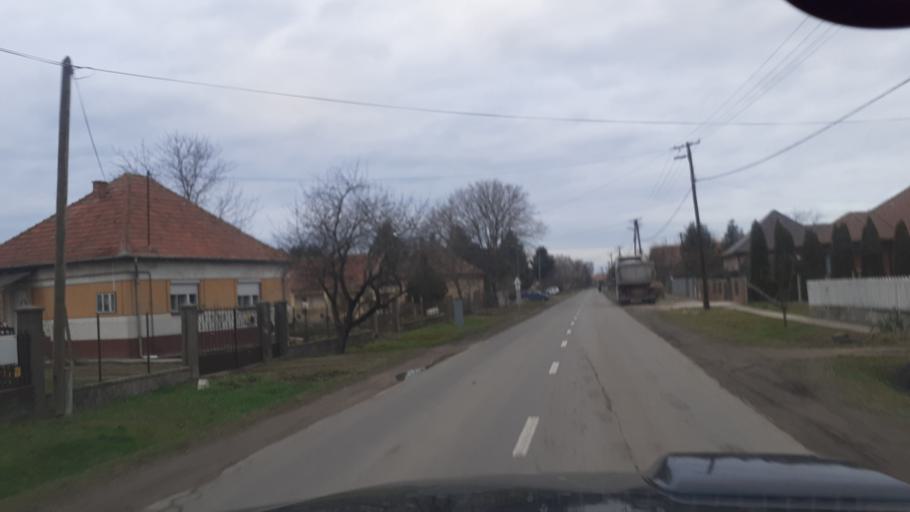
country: HU
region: Bacs-Kiskun
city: Szalkszentmarton
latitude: 46.9702
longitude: 19.0218
